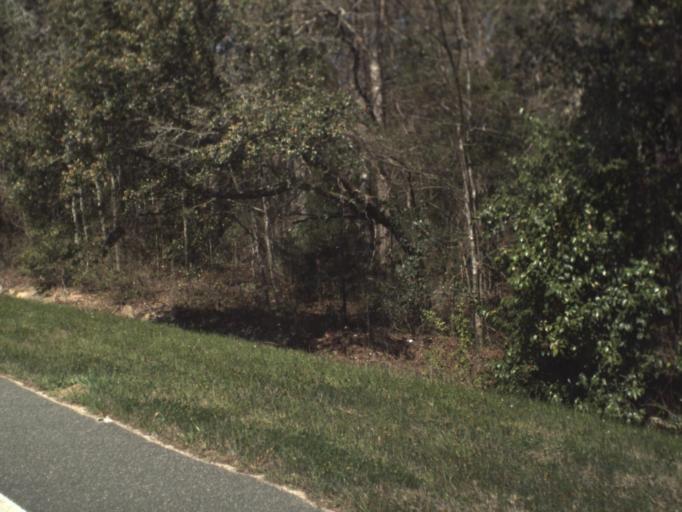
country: US
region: Florida
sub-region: Jackson County
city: Marianna
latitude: 30.7871
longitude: -85.3510
